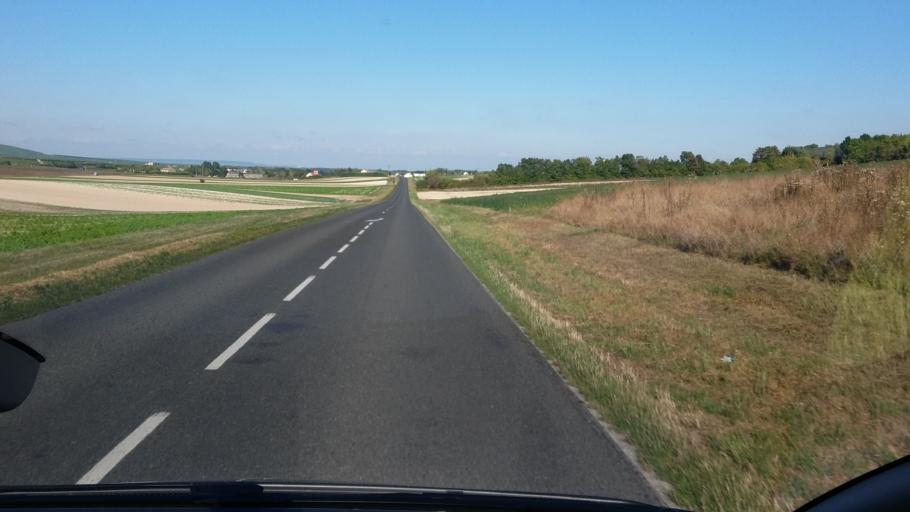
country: FR
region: Champagne-Ardenne
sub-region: Departement de la Marne
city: Vertus
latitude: 48.8663
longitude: 3.9881
